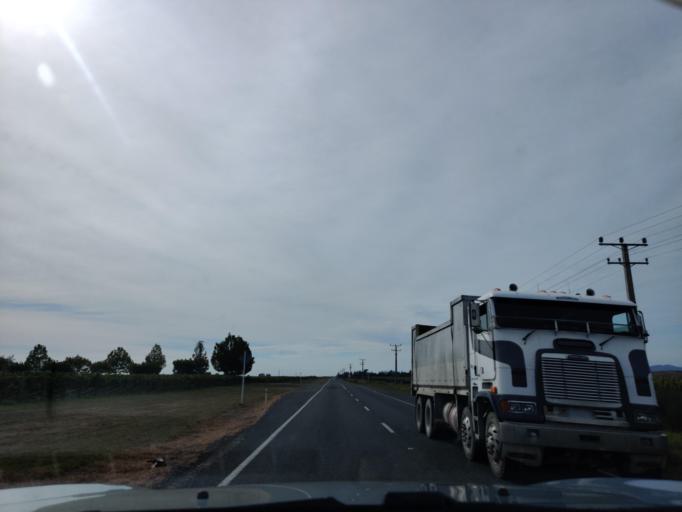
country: NZ
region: Marlborough
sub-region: Marlborough District
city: Blenheim
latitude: -41.5169
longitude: 173.7575
